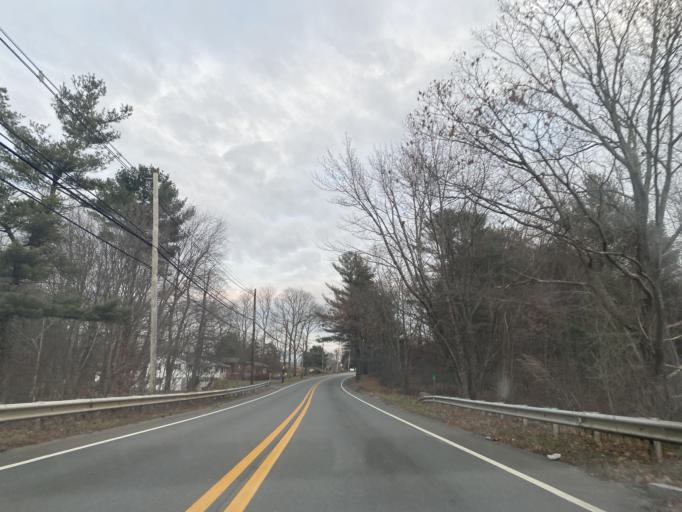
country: US
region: Massachusetts
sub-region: Worcester County
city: Spencer
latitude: 42.2557
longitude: -71.9625
